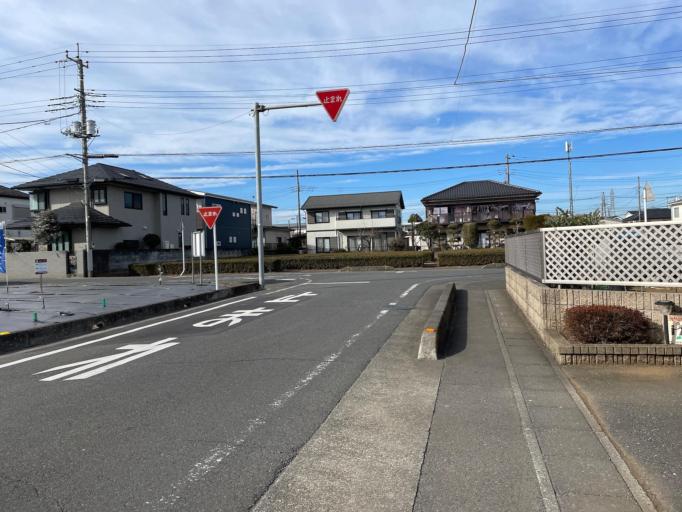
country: JP
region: Saitama
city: Sayama
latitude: 35.8297
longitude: 139.4032
